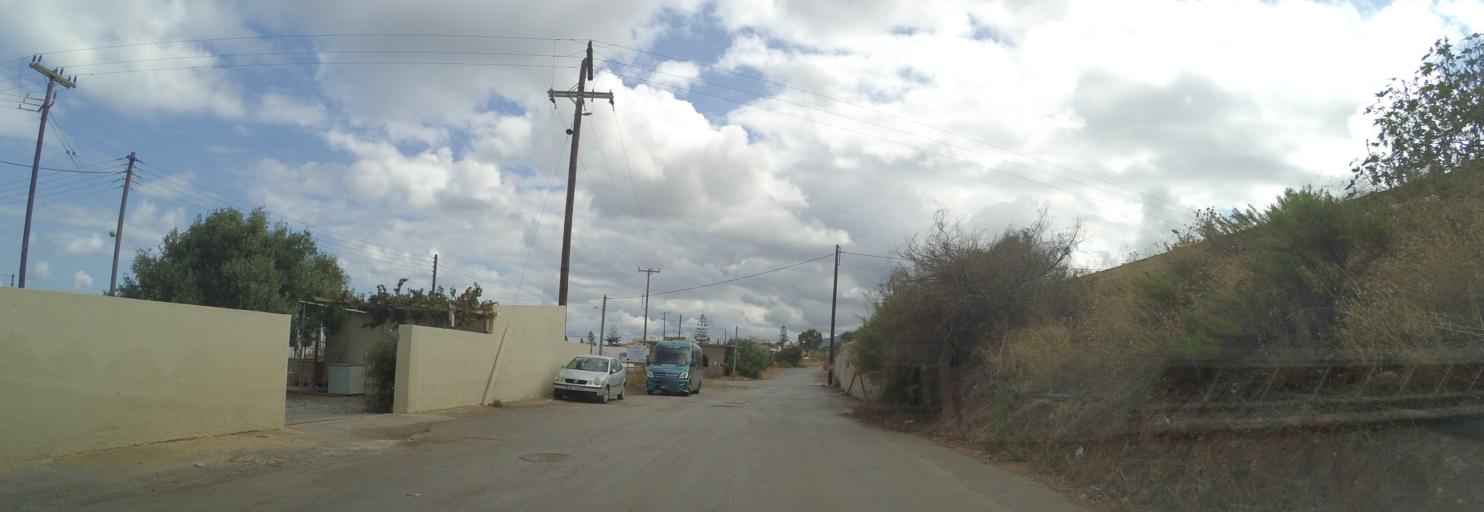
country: GR
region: Crete
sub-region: Nomos Irakleiou
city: Gournes
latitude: 35.3286
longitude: 25.2698
